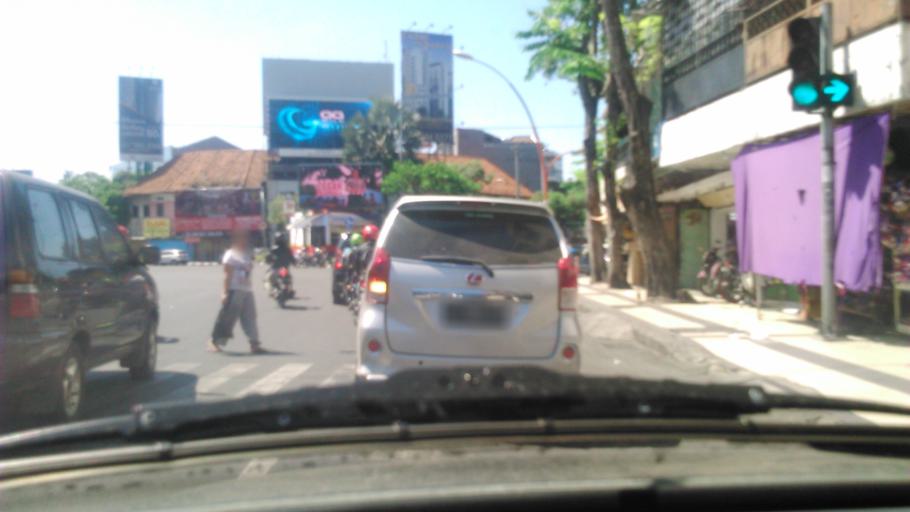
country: ID
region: East Java
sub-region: Kota Surabaya
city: Surabaya
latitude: -7.2565
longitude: 112.7341
